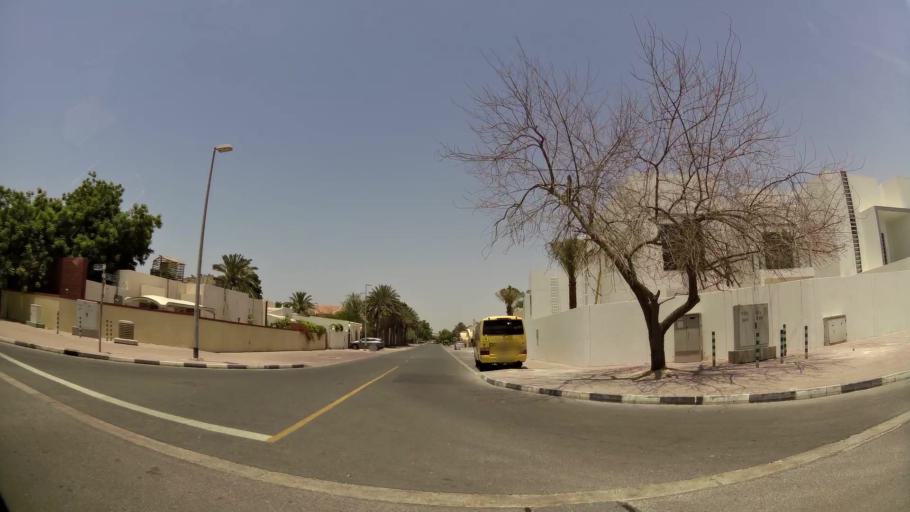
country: AE
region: Dubai
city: Dubai
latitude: 25.2215
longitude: 55.2598
